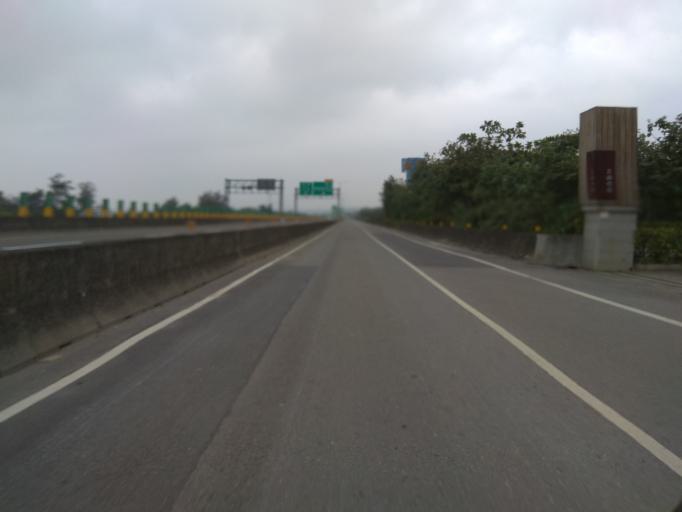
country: TW
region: Taiwan
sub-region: Hsinchu
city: Hsinchu
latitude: 24.7383
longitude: 120.8892
